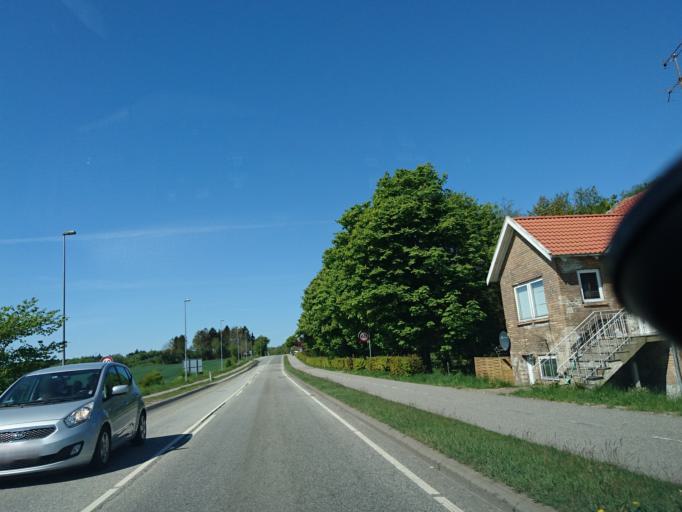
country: DK
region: North Denmark
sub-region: Hjorring Kommune
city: Sindal
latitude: 57.4705
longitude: 10.1951
